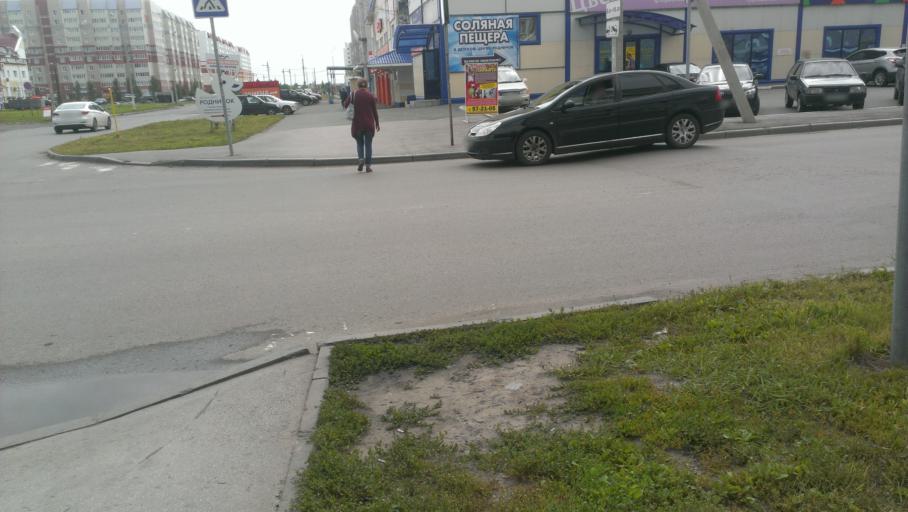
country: RU
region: Altai Krai
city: Novosilikatnyy
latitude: 53.3308
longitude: 83.6757
